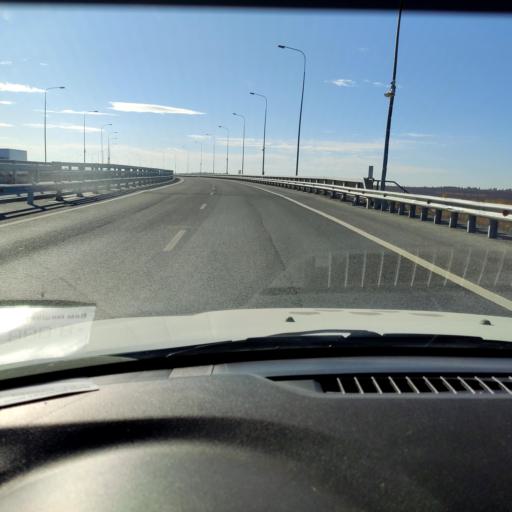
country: RU
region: Samara
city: Bereza
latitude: 53.5013
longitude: 50.1167
